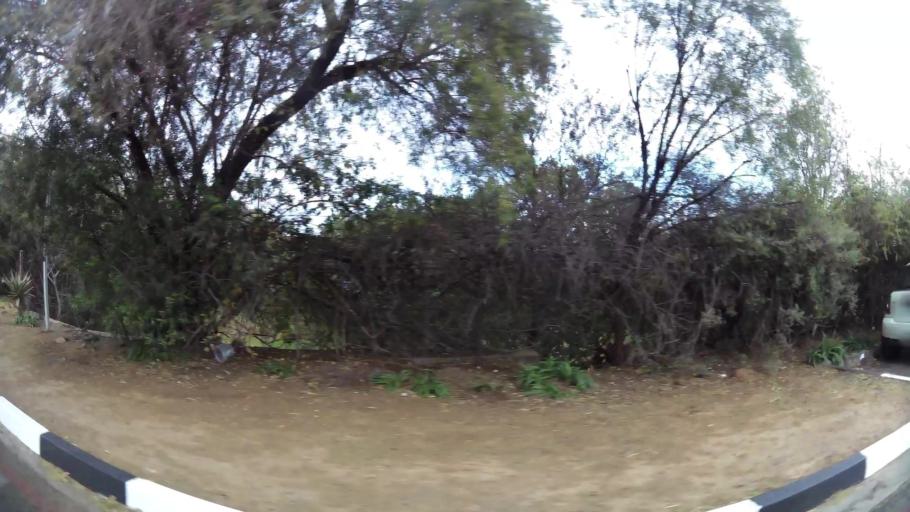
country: ZA
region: Orange Free State
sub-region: Mangaung Metropolitan Municipality
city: Bloemfontein
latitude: -29.1091
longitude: 26.1849
